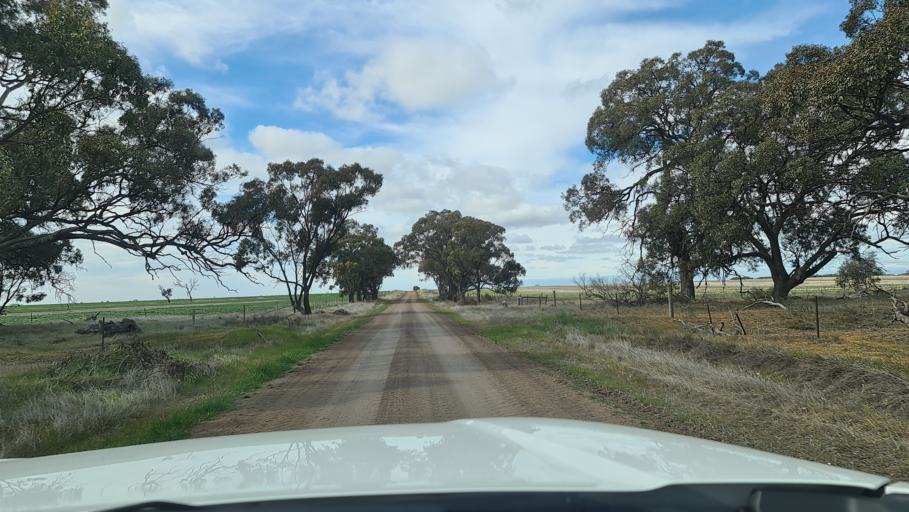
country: AU
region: Victoria
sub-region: Horsham
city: Horsham
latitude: -36.6313
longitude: 142.4154
